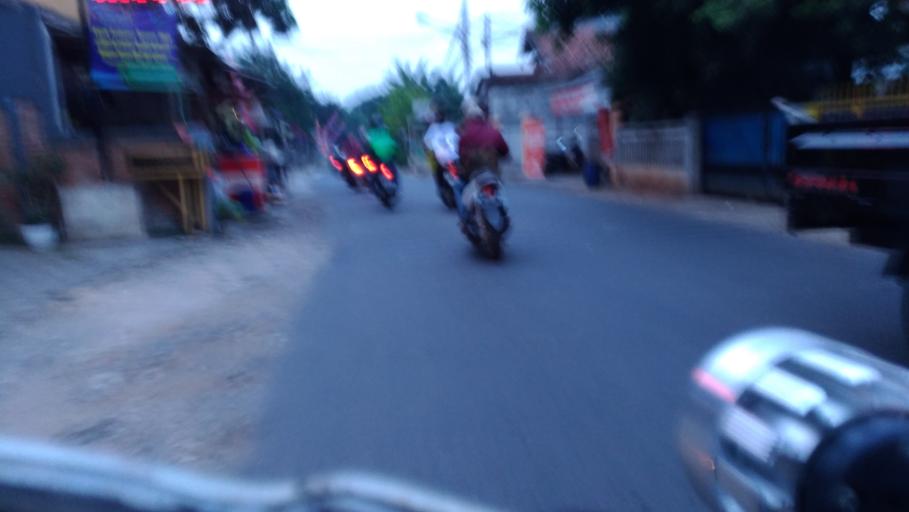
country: ID
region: West Java
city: Depok
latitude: -6.3638
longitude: 106.8846
